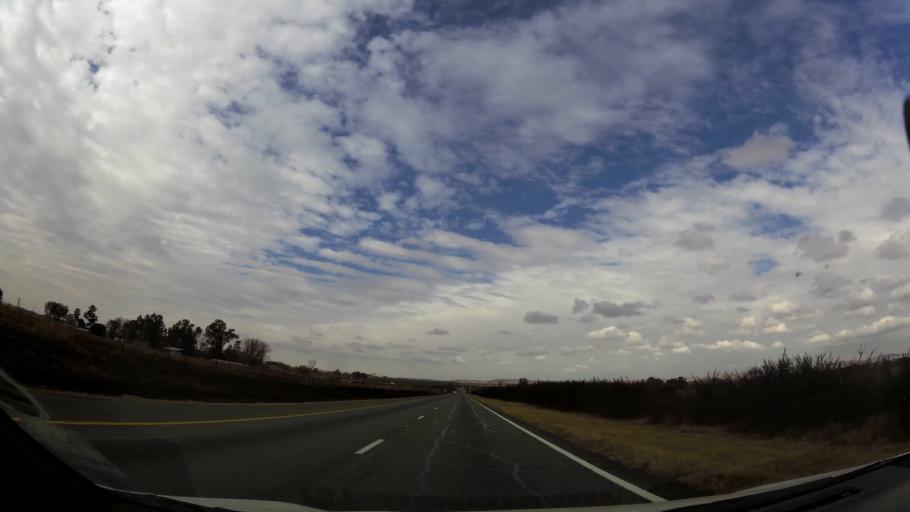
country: ZA
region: Gauteng
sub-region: Ekurhuleni Metropolitan Municipality
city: Germiston
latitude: -26.3691
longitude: 28.2399
